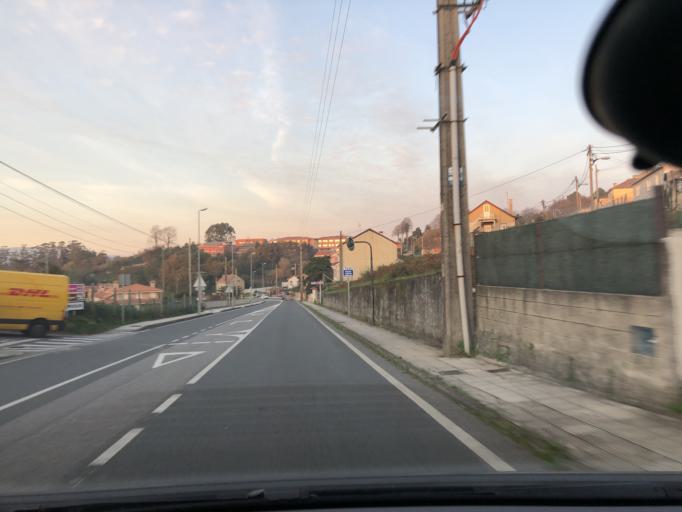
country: ES
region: Galicia
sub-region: Provincia de Pontevedra
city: Marin
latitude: 42.3864
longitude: -8.7127
